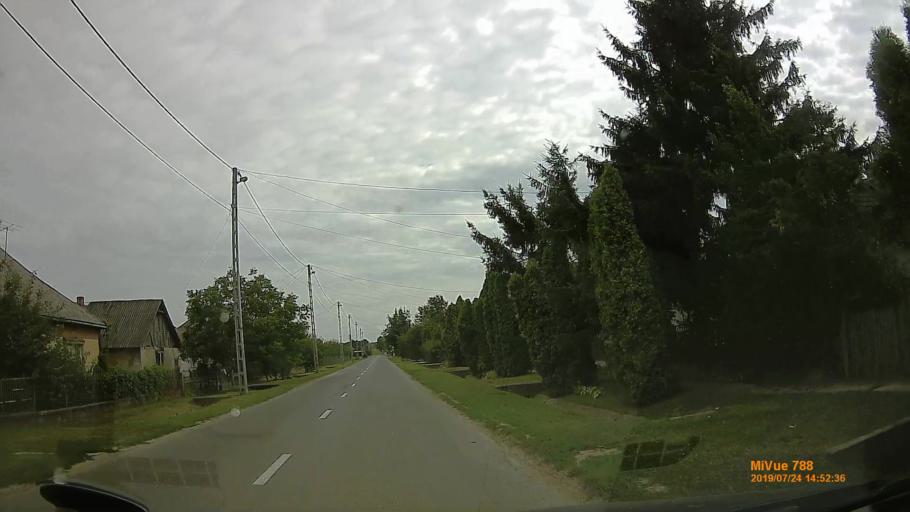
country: HU
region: Szabolcs-Szatmar-Bereg
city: Aranyosapati
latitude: 48.2611
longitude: 22.2886
